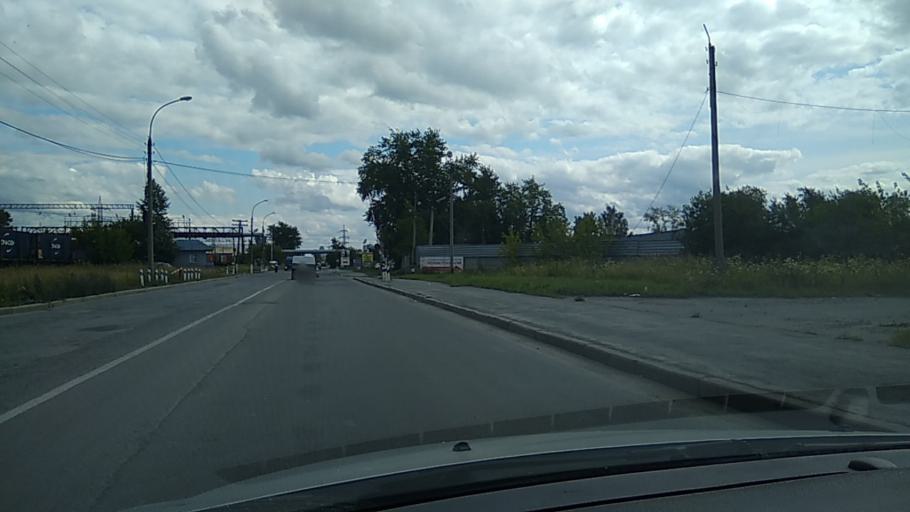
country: RU
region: Sverdlovsk
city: Yekaterinburg
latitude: 56.8814
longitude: 60.5473
